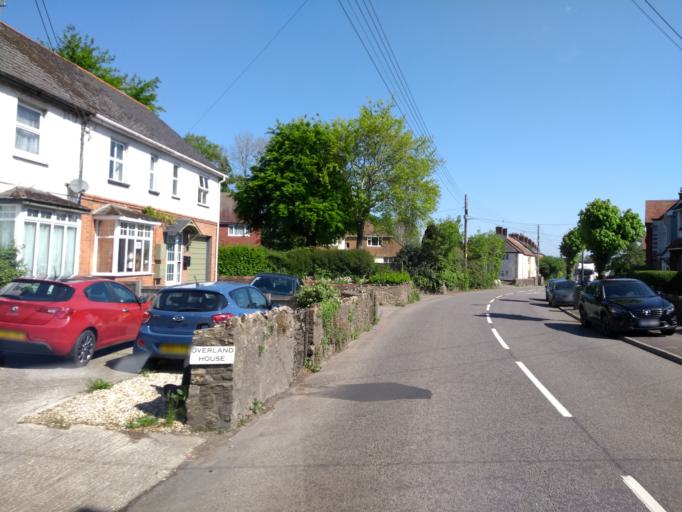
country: GB
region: England
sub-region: Somerset
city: Chard
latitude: 50.8751
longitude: -2.9595
